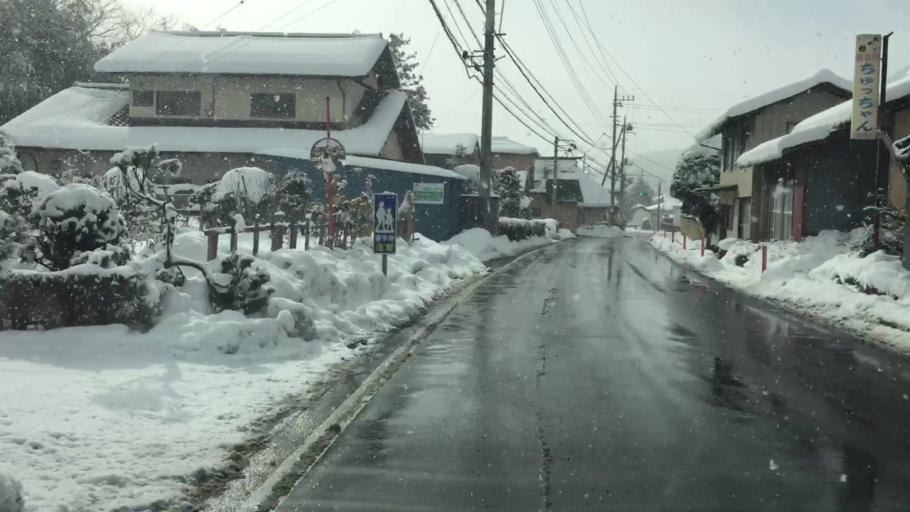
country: JP
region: Gunma
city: Numata
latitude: 36.6969
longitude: 139.0647
